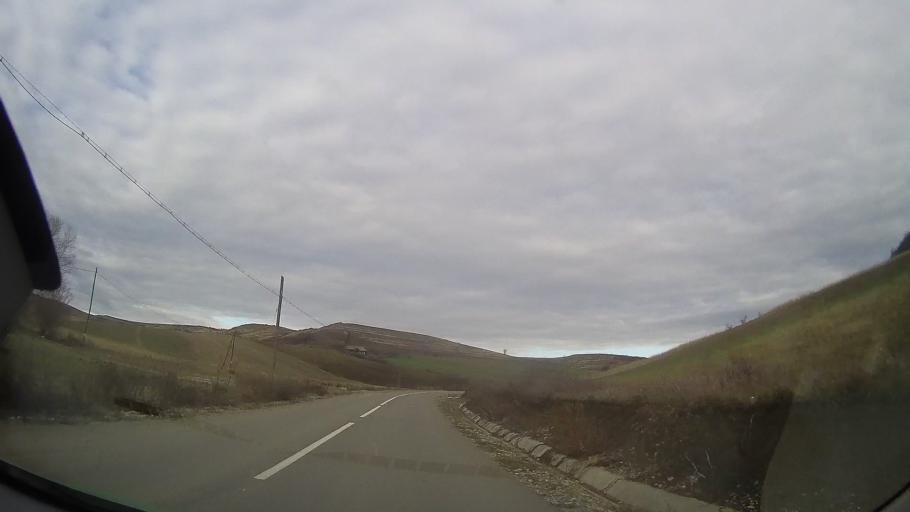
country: RO
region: Bistrita-Nasaud
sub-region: Comuna Silvasu de Campie
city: Silvasu de Campie
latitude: 46.8177
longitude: 24.2968
